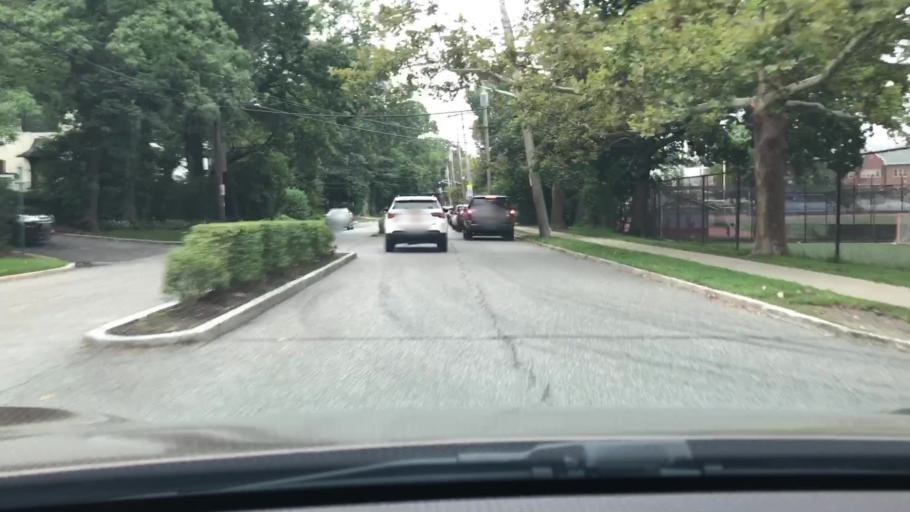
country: US
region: New York
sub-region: Westchester County
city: Bronxville
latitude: 40.9395
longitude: -73.8277
